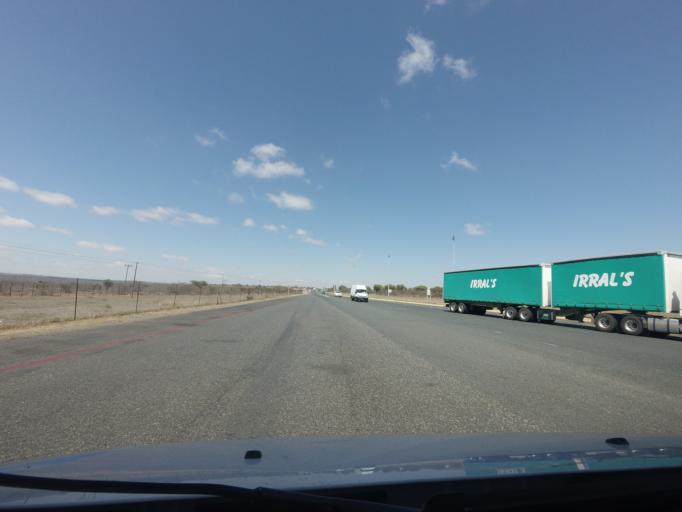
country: ZA
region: Limpopo
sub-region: Vhembe District Municipality
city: Louis Trichardt
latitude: -23.3676
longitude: 29.7745
